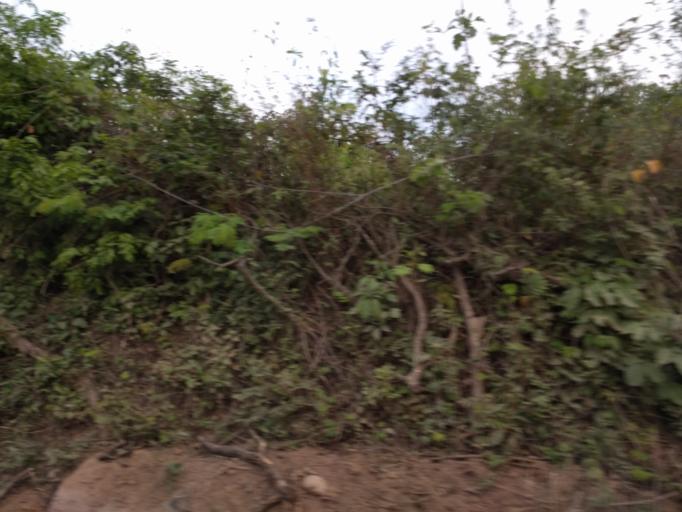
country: BO
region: Santa Cruz
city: Santa Rita
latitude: -17.9294
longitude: -63.3875
